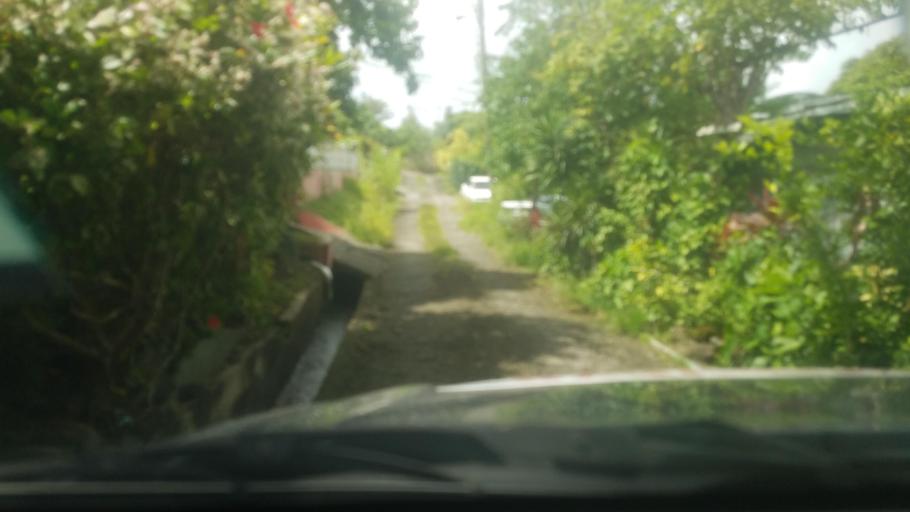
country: LC
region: Laborie Quarter
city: Laborie
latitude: 13.7485
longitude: -60.9951
